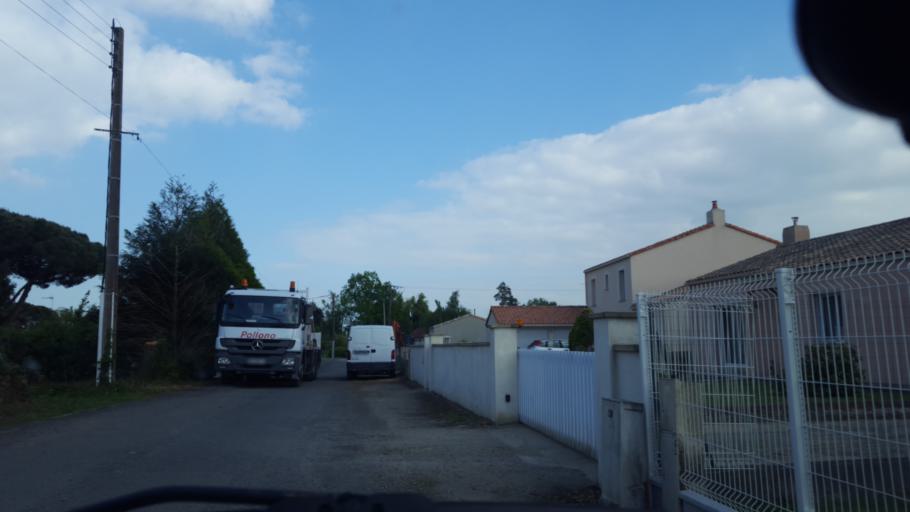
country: FR
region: Pays de la Loire
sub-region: Departement de la Loire-Atlantique
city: Saint-Philbert-de-Grand-Lieu
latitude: 47.0334
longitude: -1.6078
